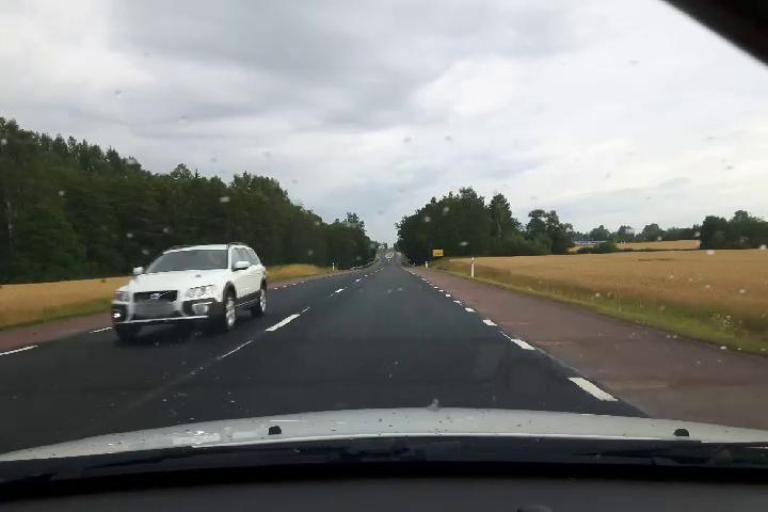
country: SE
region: Uppsala
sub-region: Osthammars Kommun
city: Bjorklinge
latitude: 59.9589
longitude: 17.5841
